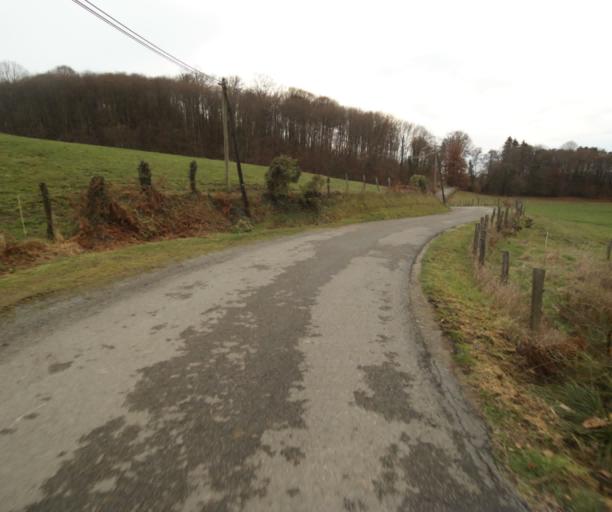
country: FR
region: Limousin
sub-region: Departement de la Correze
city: Chameyrat
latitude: 45.2576
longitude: 1.6777
